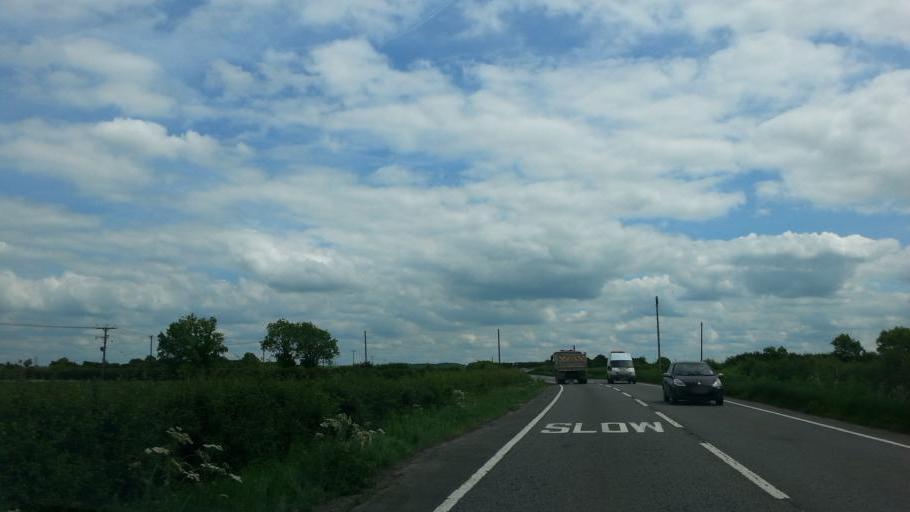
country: GB
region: England
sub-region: Lincolnshire
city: Long Bennington
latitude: 52.9339
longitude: -0.7522
